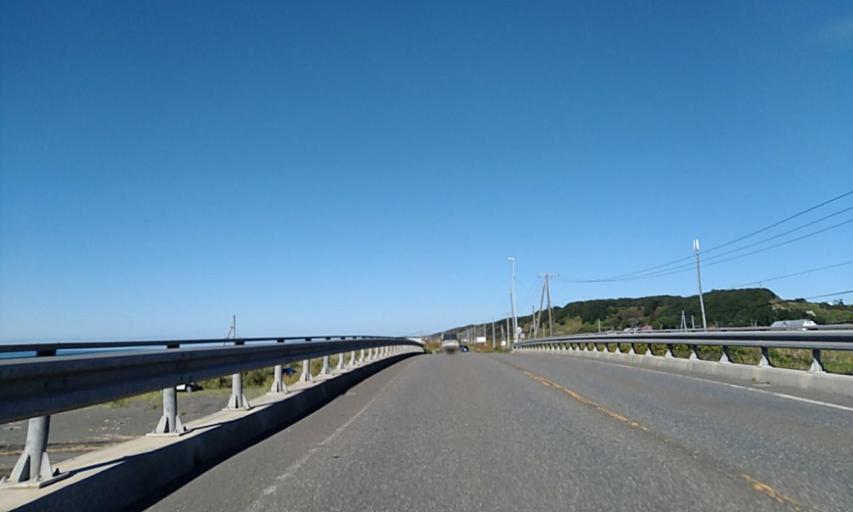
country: JP
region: Hokkaido
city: Shizunai-furukawacho
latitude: 42.4597
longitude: 142.1695
